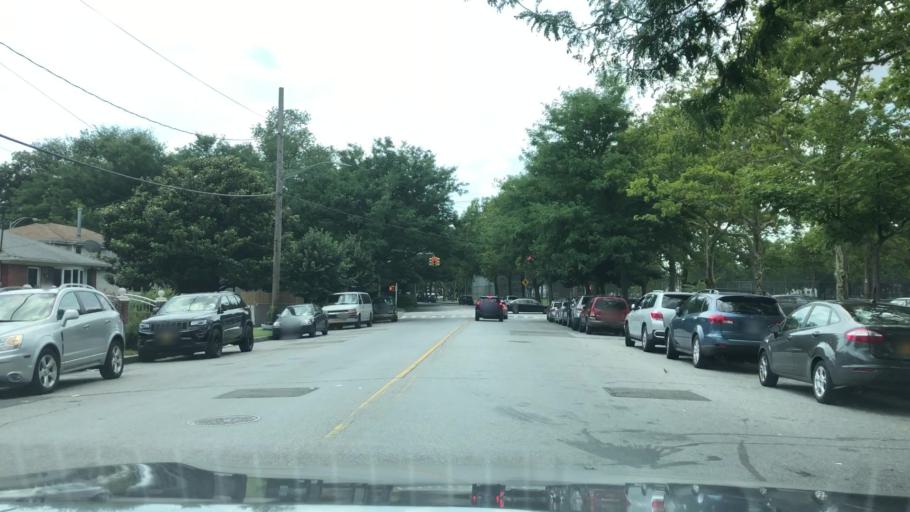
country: US
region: New York
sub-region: Queens County
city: Jamaica
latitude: 40.6840
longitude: -73.7838
